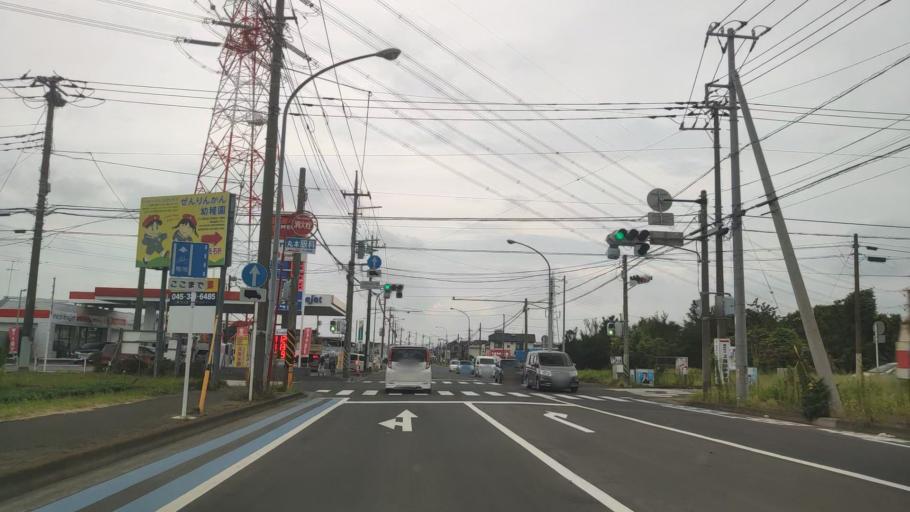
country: JP
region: Kanagawa
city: Minami-rinkan
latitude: 35.4308
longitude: 139.4846
